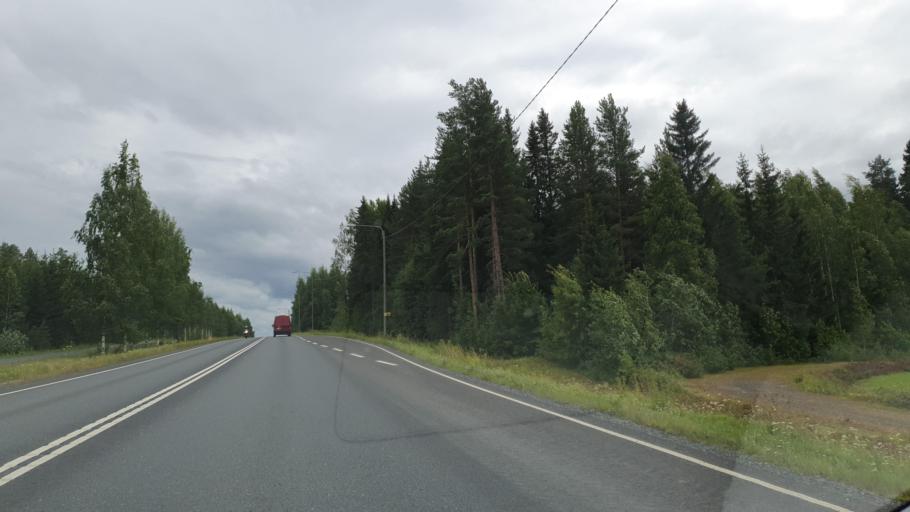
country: FI
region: Northern Savo
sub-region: Ylae-Savo
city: Lapinlahti
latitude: 63.4335
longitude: 27.3268
